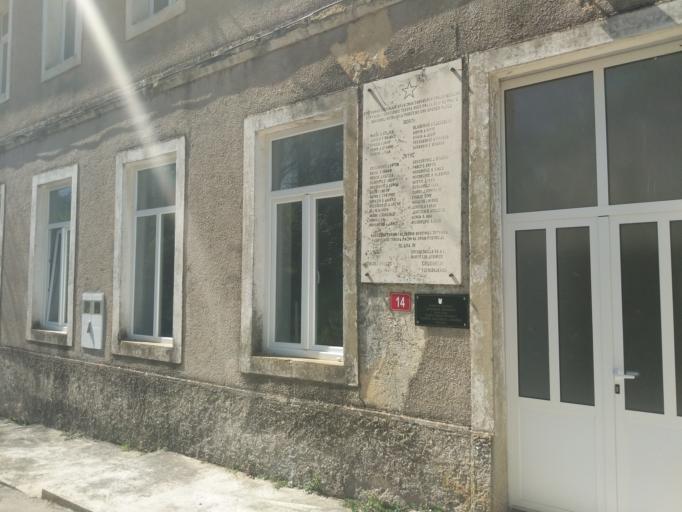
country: HR
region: Istarska
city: Pazin
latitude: 45.2811
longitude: 13.9426
